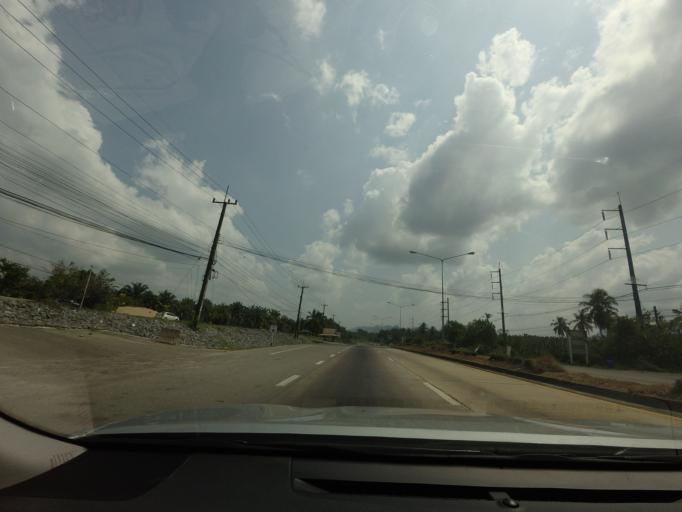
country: TH
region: Phangnga
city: Thap Put
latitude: 8.5068
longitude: 98.6828
